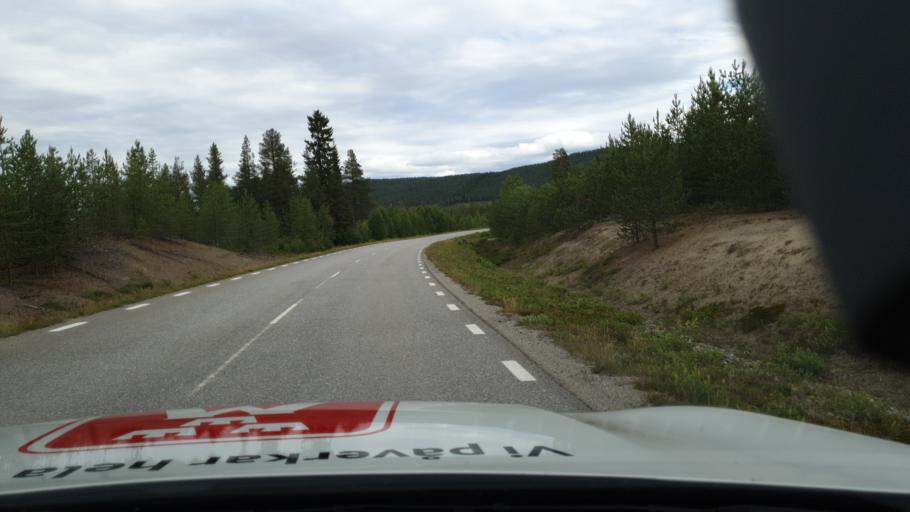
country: SE
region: Vaesterbotten
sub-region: Sorsele Kommun
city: Sorsele
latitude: 65.5395
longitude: 17.3981
